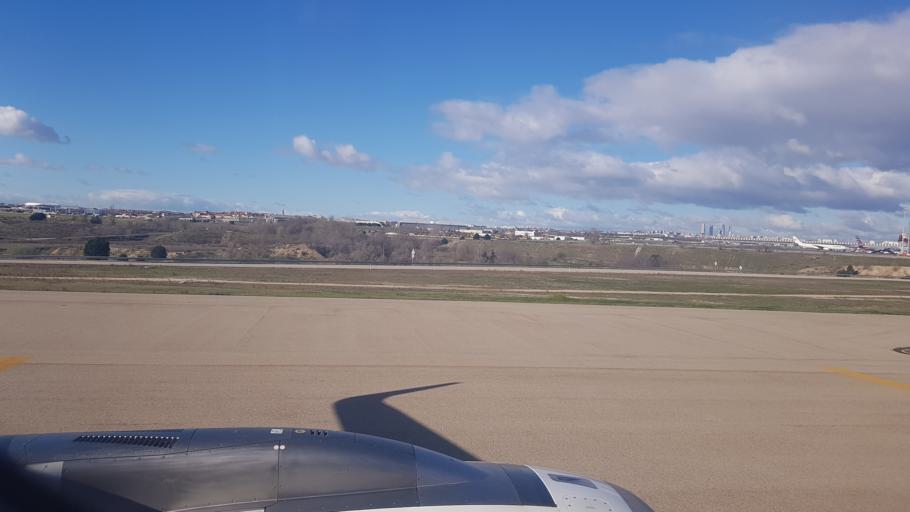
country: ES
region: Madrid
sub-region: Provincia de Madrid
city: Barajas de Madrid
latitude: 40.4894
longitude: -3.5552
